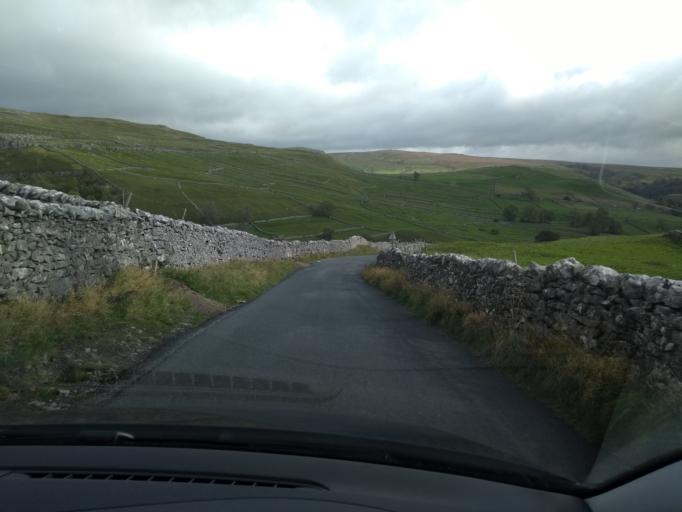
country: GB
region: England
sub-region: North Yorkshire
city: Gargrave
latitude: 54.0690
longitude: -2.1638
